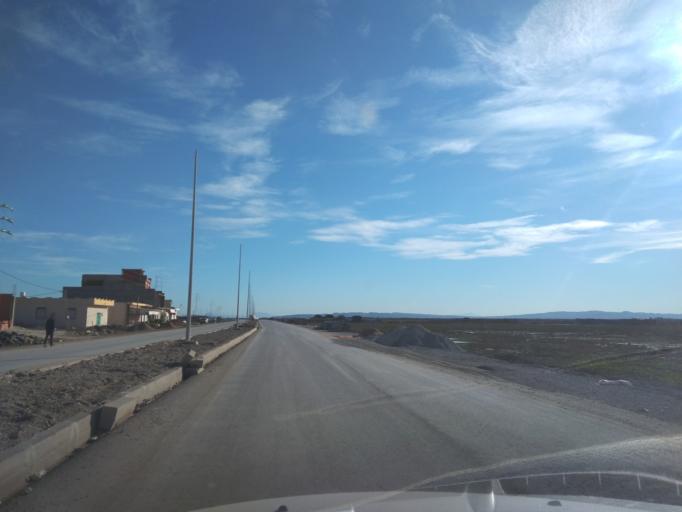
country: TN
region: Ariana
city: Qal'at al Andalus
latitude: 37.0512
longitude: 10.1230
